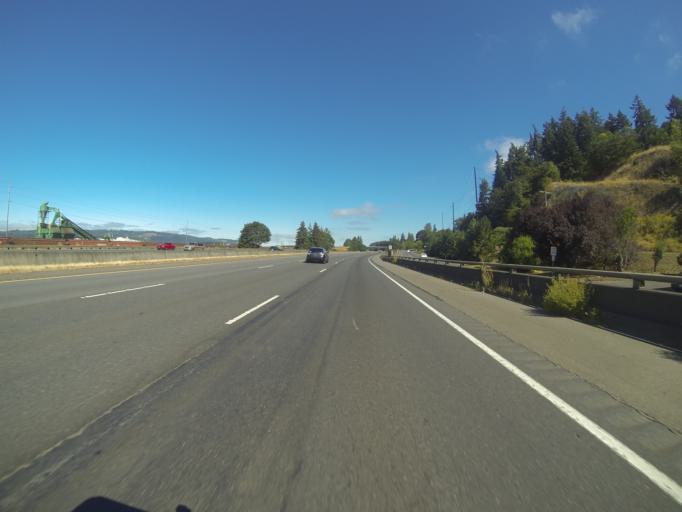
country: US
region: Washington
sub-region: Cowlitz County
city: Kalama
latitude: 46.0142
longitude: -122.8482
